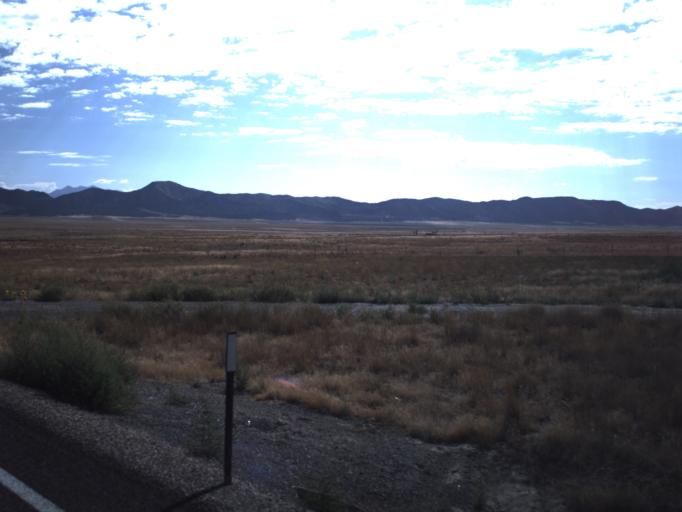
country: US
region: Utah
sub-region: Juab County
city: Mona
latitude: 39.7033
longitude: -112.2158
